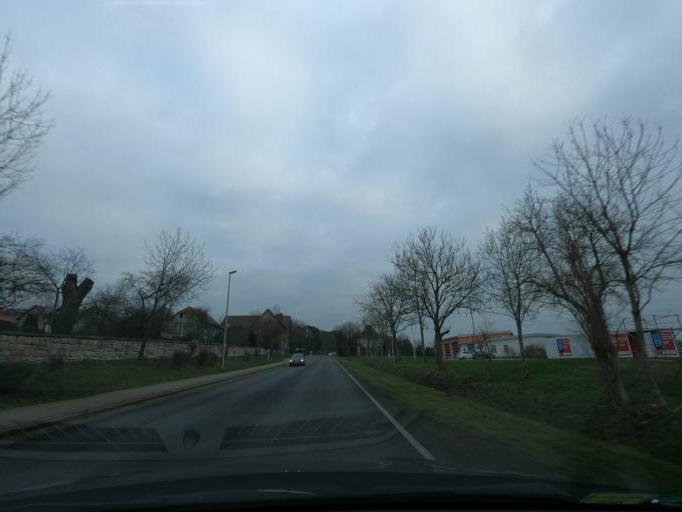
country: DE
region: Lower Saxony
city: Wittmar
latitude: 52.1431
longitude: 10.6116
